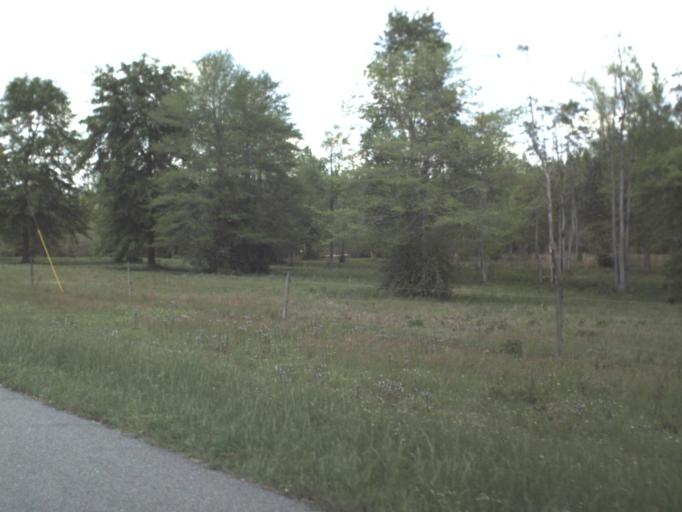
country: US
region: Florida
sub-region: Escambia County
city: Molino
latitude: 30.7825
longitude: -87.4040
